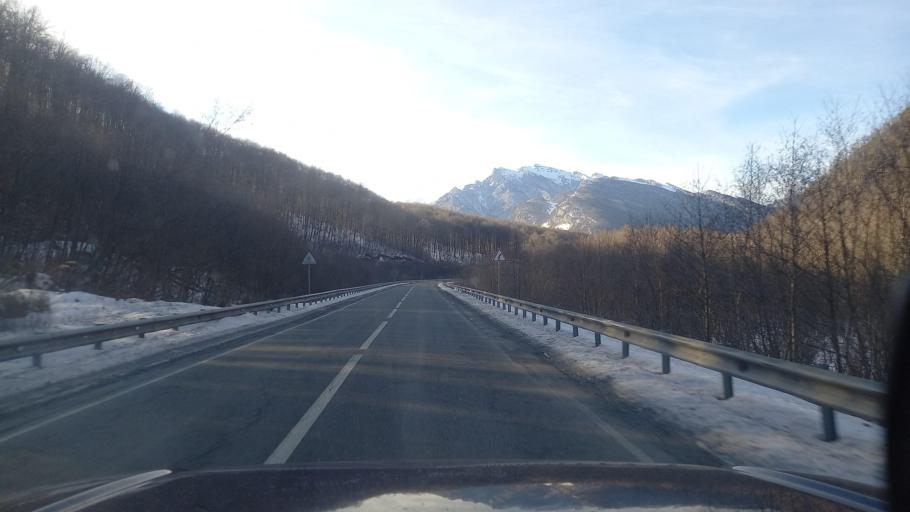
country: RU
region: North Ossetia
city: Gizel'
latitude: 42.9385
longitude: 44.5578
